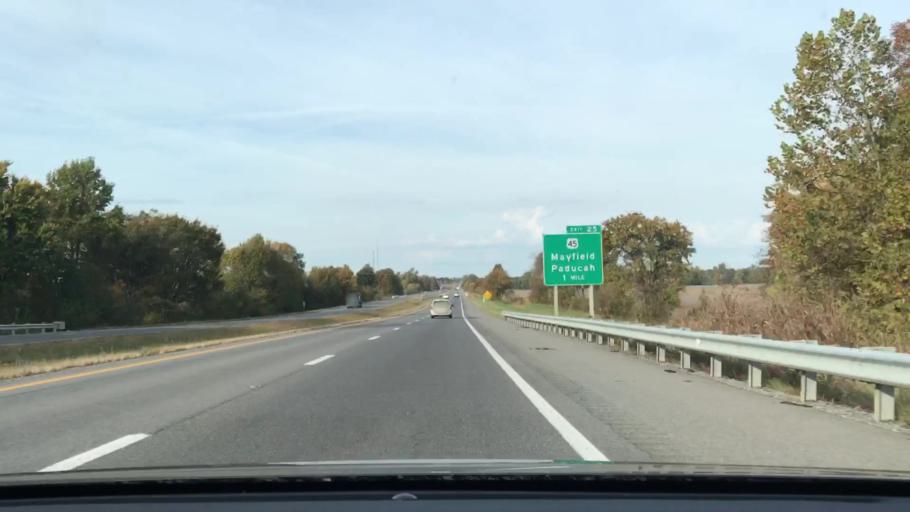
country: US
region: Kentucky
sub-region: Graves County
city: Mayfield
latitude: 36.7697
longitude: -88.6190
